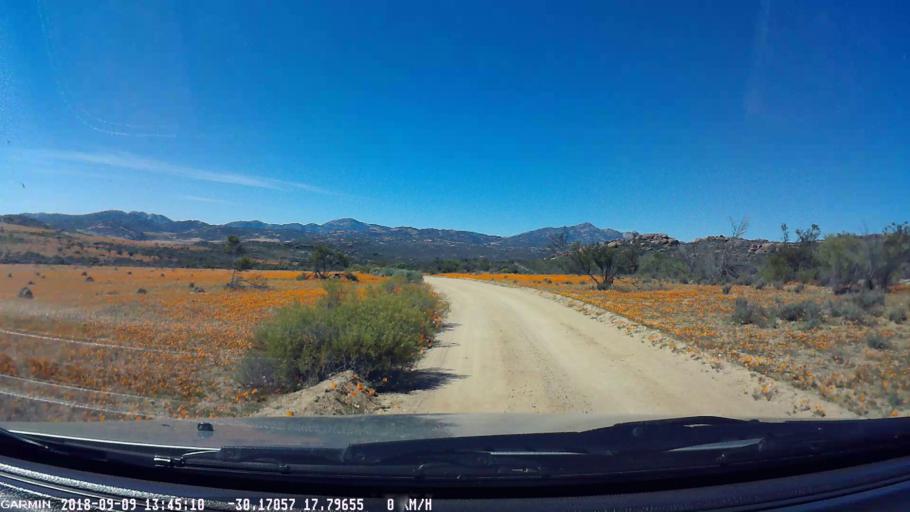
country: ZA
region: Northern Cape
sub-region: Namakwa District Municipality
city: Garies
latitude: -30.1706
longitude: 17.7965
